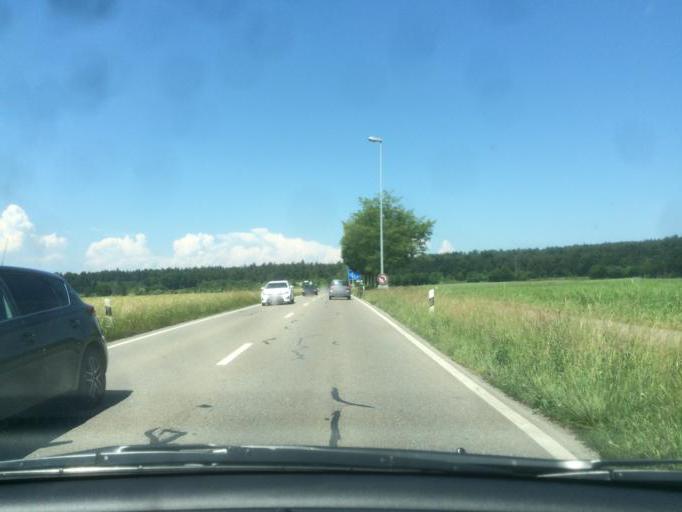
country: CH
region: Zurich
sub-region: Bezirk Uster
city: Uster / Gschwader
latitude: 47.3631
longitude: 8.7109
